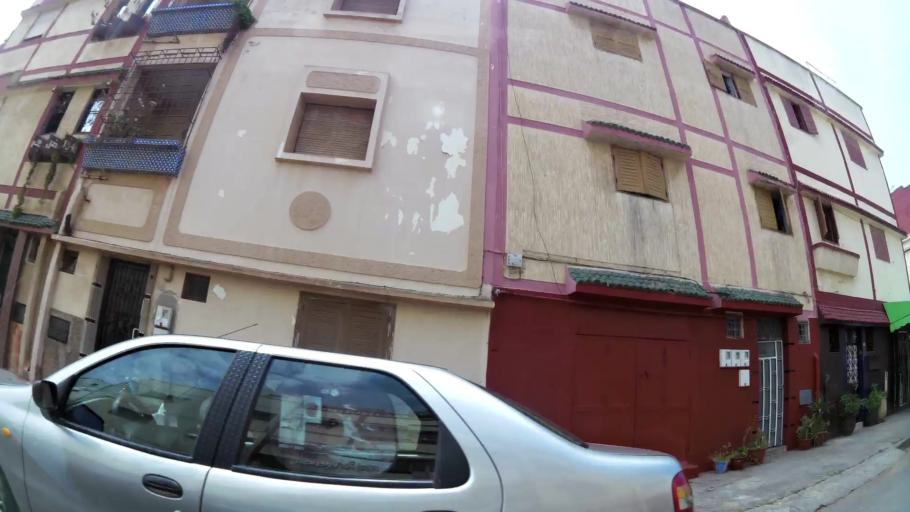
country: MA
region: Rabat-Sale-Zemmour-Zaer
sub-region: Skhirate-Temara
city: Temara
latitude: 33.9834
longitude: -6.8903
